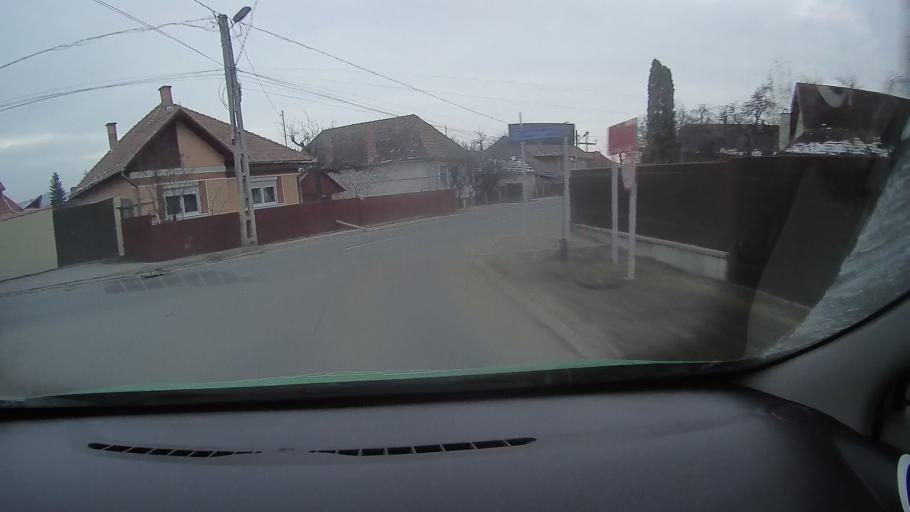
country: RO
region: Harghita
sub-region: Municipiul Odorheiu Secuiesc
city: Odorheiu Secuiesc
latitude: 46.3092
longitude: 25.2859
